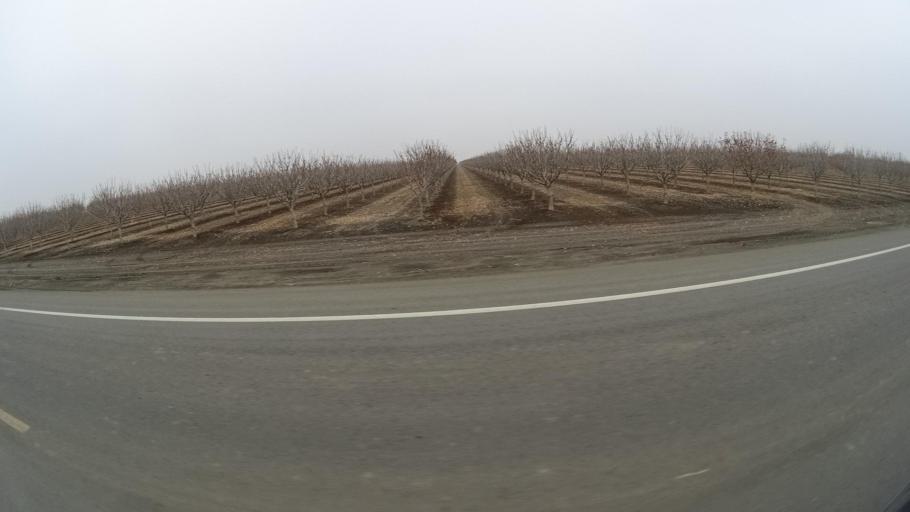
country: US
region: California
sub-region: Kern County
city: Buttonwillow
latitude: 35.3691
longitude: -119.4710
